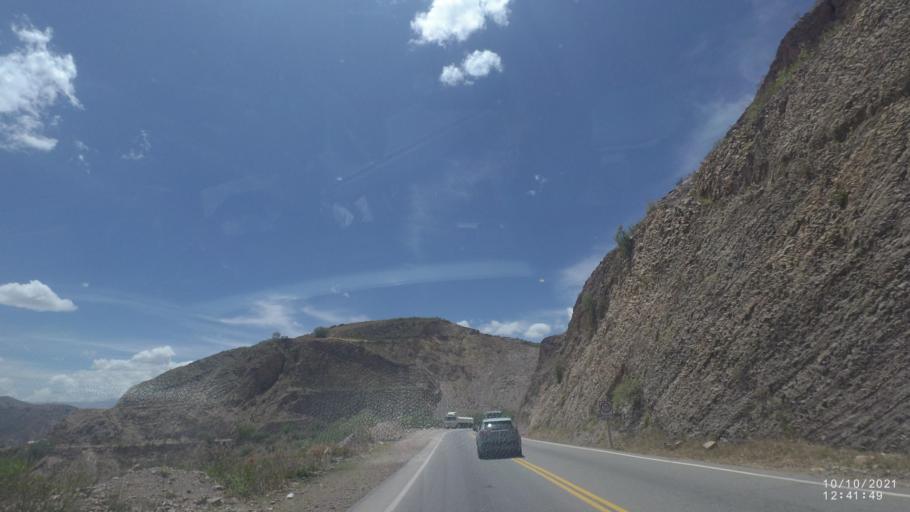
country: BO
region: Cochabamba
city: Irpa Irpa
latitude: -17.6329
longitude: -66.3904
